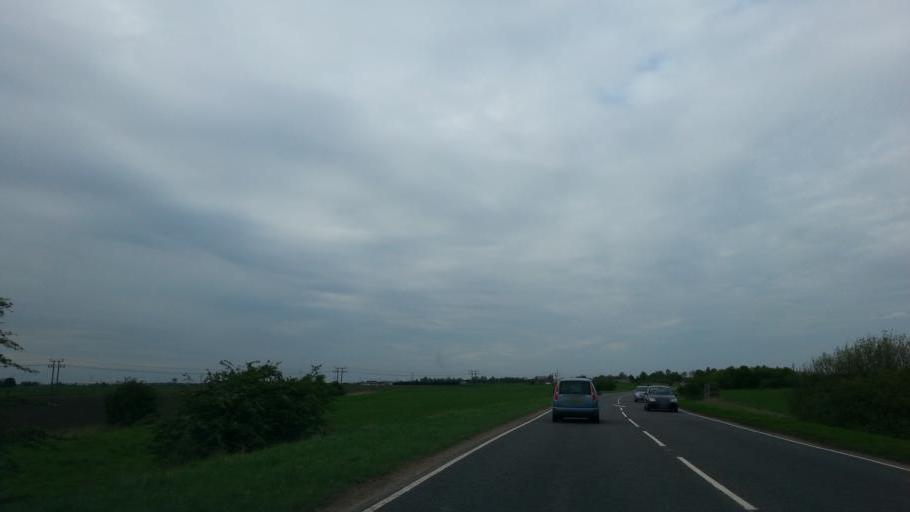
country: GB
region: England
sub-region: Cambridgeshire
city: March
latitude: 52.5359
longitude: 0.0694
